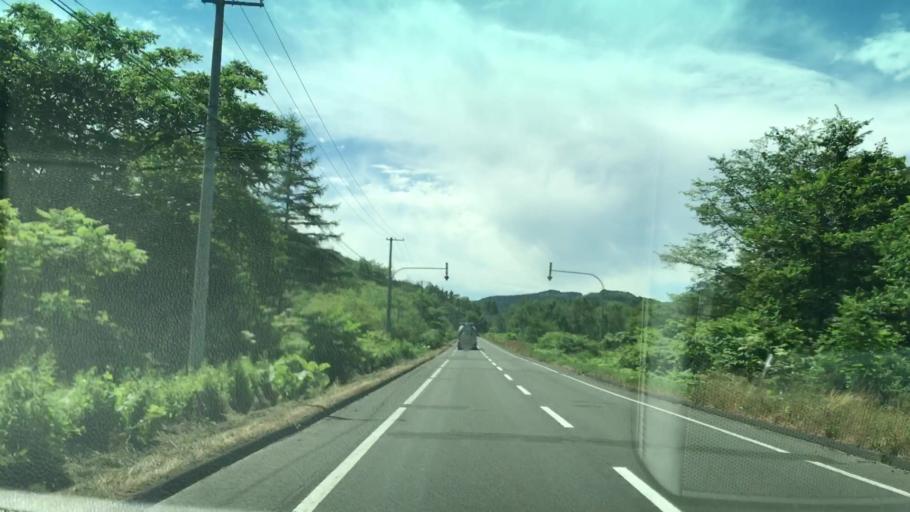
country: JP
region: Hokkaido
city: Shimo-furano
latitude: 42.9377
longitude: 142.4450
